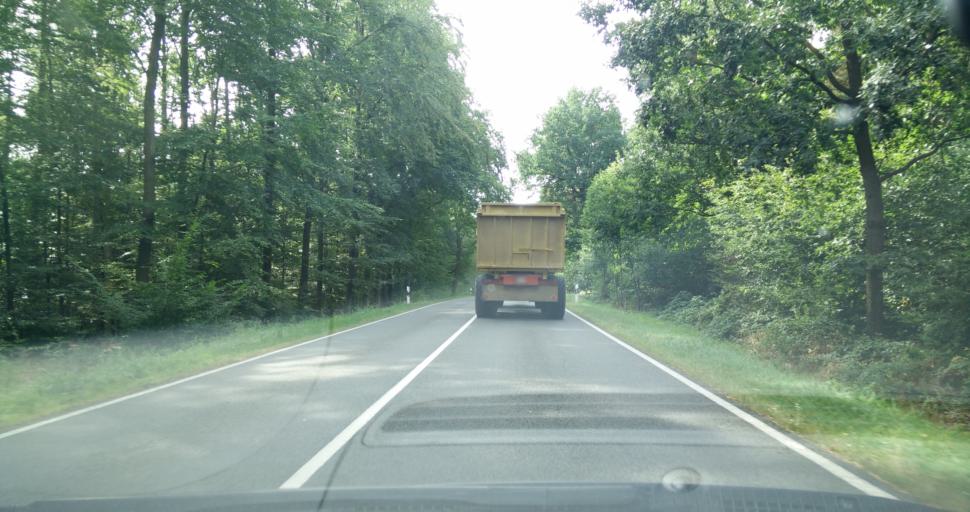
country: DE
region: Saxony
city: Grossbothen
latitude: 51.1372
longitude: 12.7337
